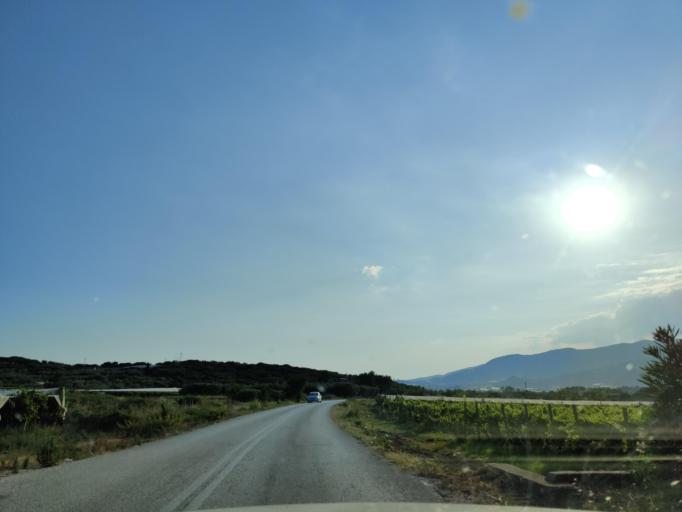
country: GR
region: East Macedonia and Thrace
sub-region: Nomos Kavalas
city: Nea Peramos
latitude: 40.8262
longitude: 24.2930
